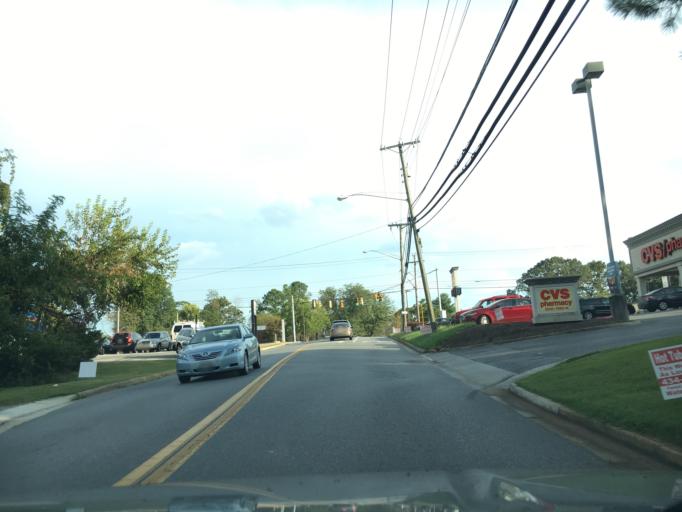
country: US
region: Virginia
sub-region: City of Lynchburg
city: West Lynchburg
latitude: 37.4156
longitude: -79.2077
